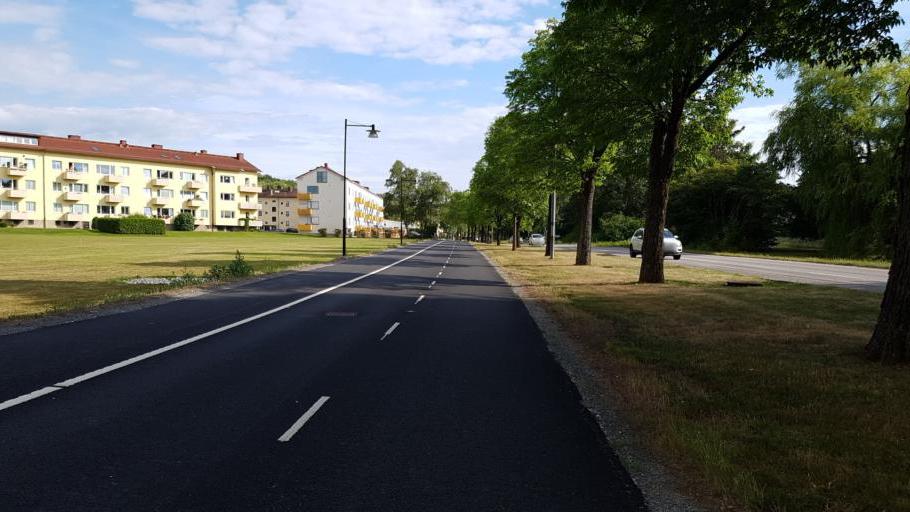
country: SE
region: Vaestra Goetaland
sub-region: Molndal
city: Moelndal
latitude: 57.7083
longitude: 12.0241
